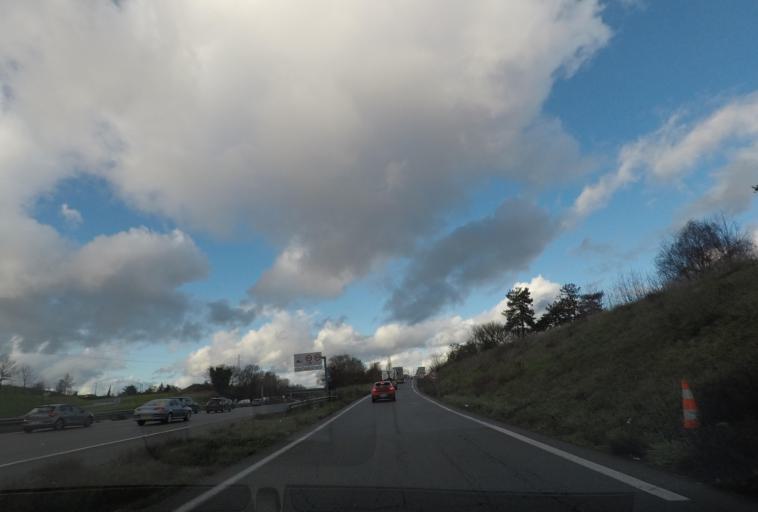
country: FR
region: Ile-de-France
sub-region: Departement de l'Essonne
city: Ormoy
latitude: 48.5700
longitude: 2.4704
